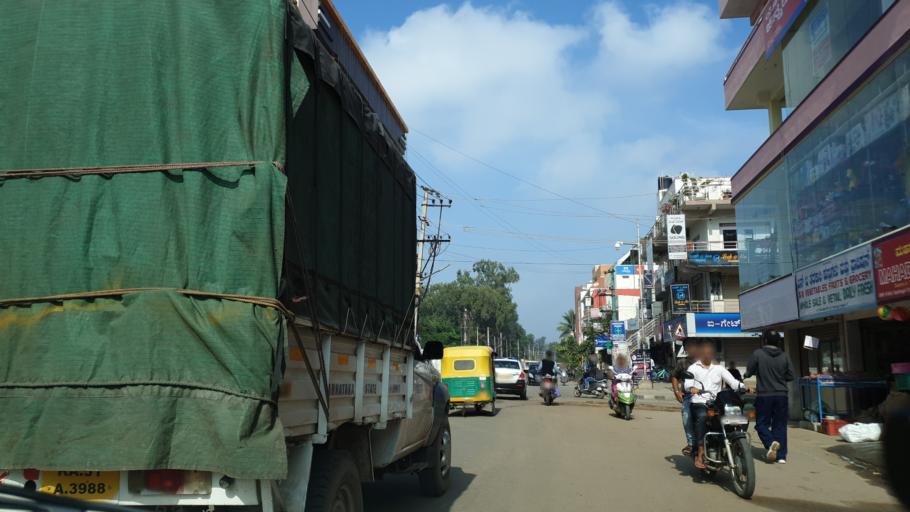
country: IN
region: Karnataka
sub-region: Bangalore Urban
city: Bangalore
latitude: 12.9727
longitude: 77.6783
